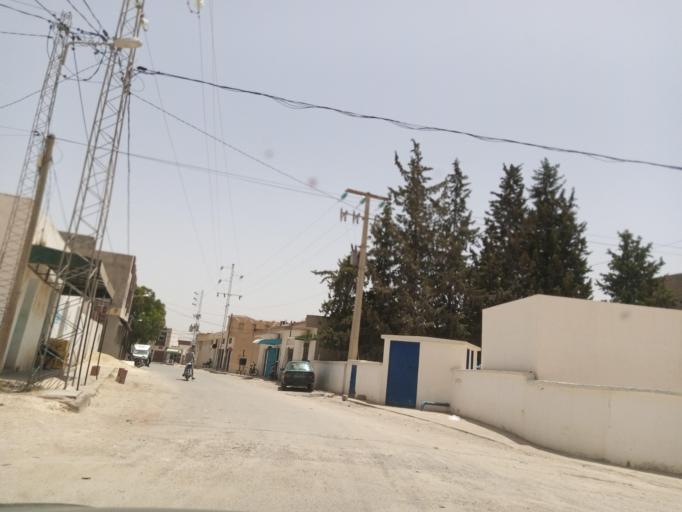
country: TN
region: Al Qasrayn
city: Kasserine
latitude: 35.2132
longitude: 8.8946
